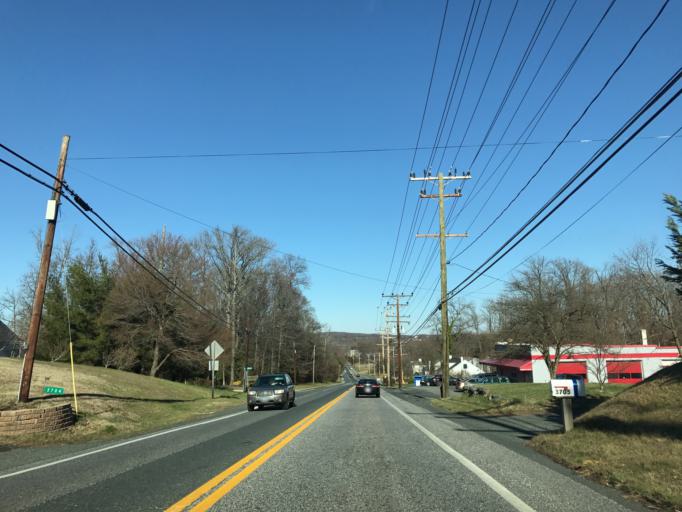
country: US
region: Maryland
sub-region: Harford County
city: Riverside
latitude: 39.4655
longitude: -76.2765
